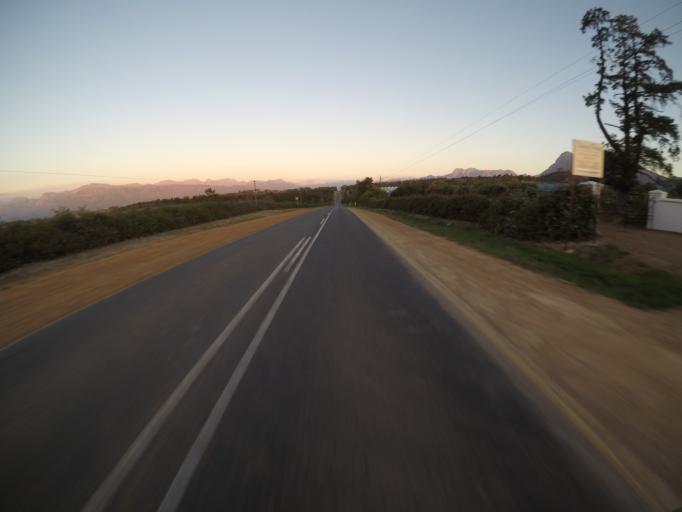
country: ZA
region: Western Cape
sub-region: Cape Winelands District Municipality
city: Paarl
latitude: -33.8060
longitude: 18.8981
